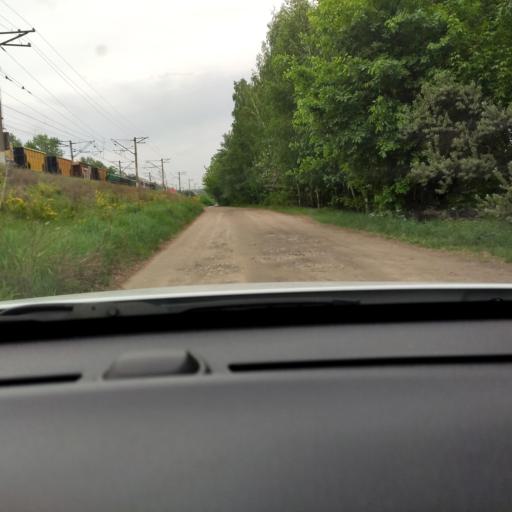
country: RU
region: Tatarstan
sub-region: Gorod Kazan'
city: Kazan
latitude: 55.8466
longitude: 49.1694
